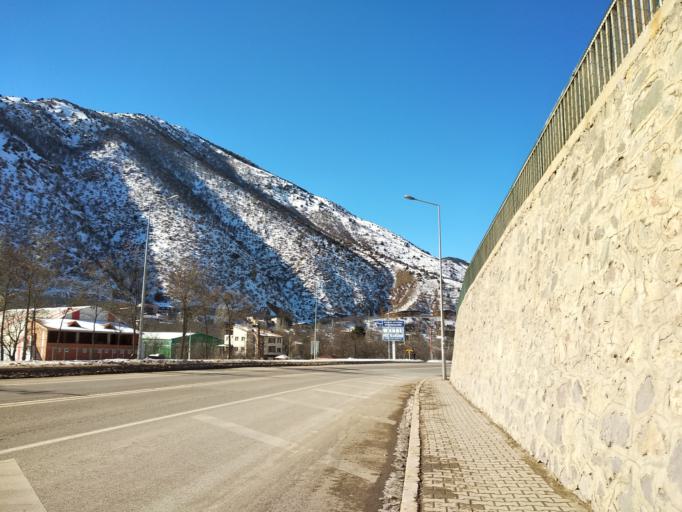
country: TR
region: Gumushane
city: Gumushkhane
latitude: 40.4367
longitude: 39.5094
